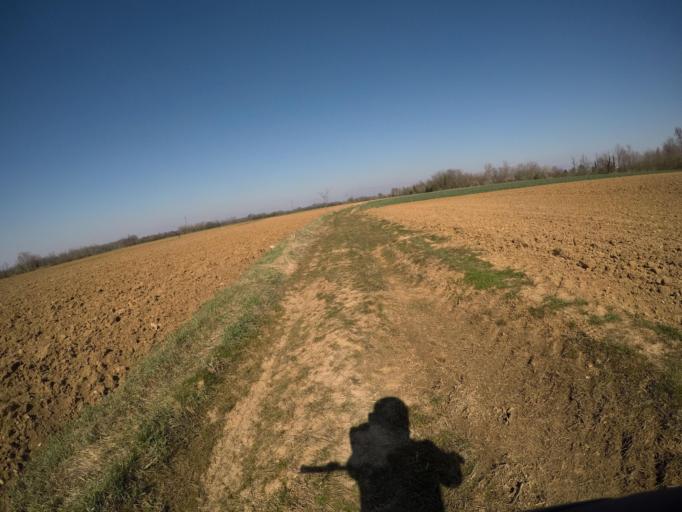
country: IT
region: Friuli Venezia Giulia
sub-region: Provincia di Udine
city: Zugliano-Terenzano-Cargnacco
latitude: 46.0105
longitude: 13.2010
